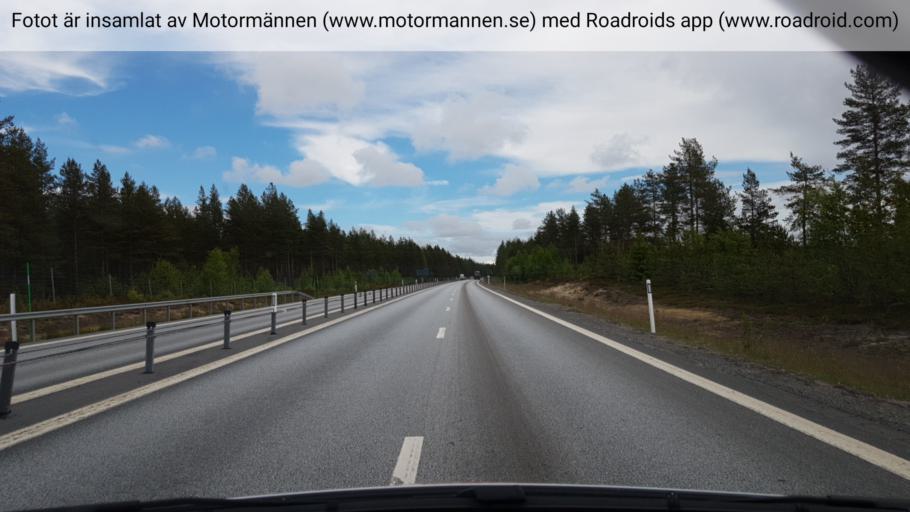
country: SE
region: Vaesterbotten
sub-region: Nordmalings Kommun
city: Nordmaling
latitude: 63.5839
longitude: 19.5478
